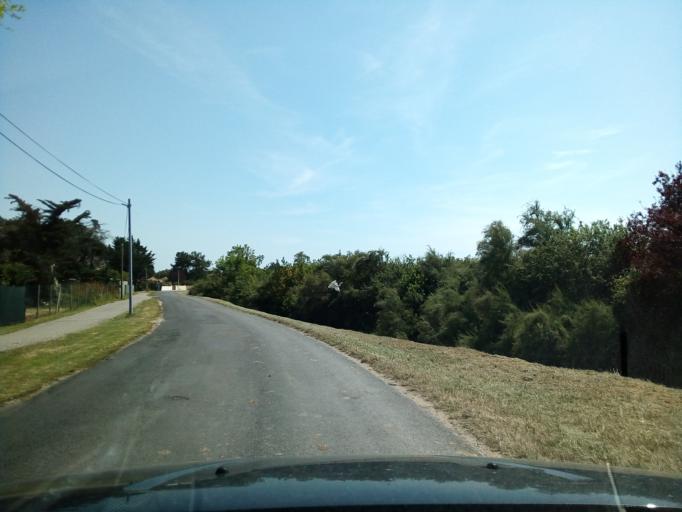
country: FR
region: Poitou-Charentes
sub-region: Departement de la Charente-Maritime
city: Boyard-Ville
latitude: 45.9766
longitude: -1.2984
